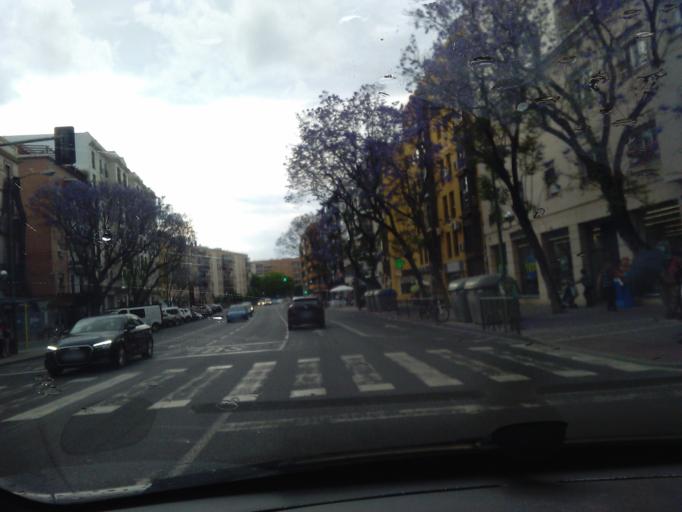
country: ES
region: Andalusia
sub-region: Provincia de Sevilla
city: Sevilla
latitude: 37.3876
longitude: -5.9795
